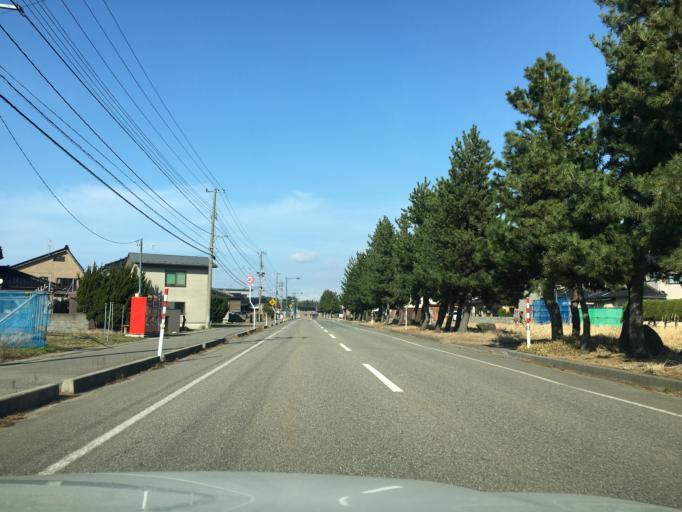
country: JP
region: Yamagata
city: Tsuruoka
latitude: 38.7890
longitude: 139.7665
